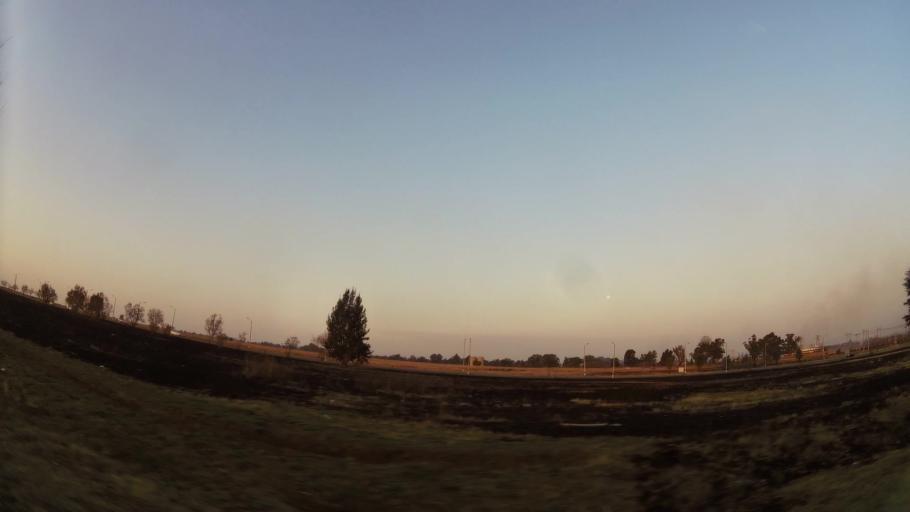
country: ZA
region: Gauteng
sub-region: Ekurhuleni Metropolitan Municipality
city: Springs
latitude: -26.3146
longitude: 28.4543
